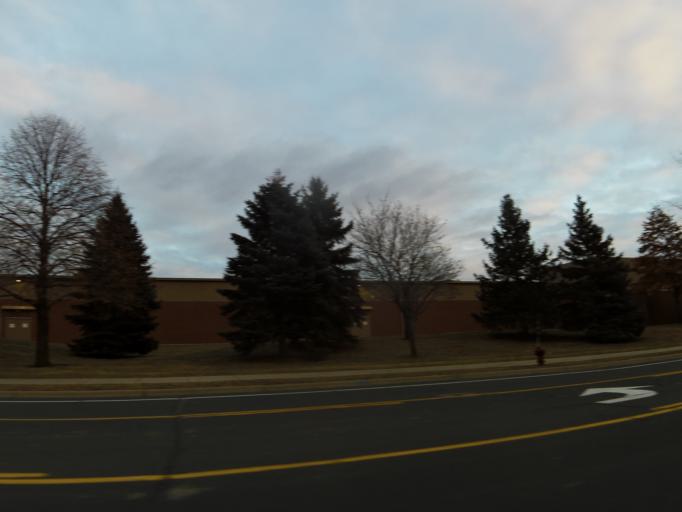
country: US
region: Minnesota
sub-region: Ramsey County
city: Vadnais Heights
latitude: 45.0492
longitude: -93.0656
